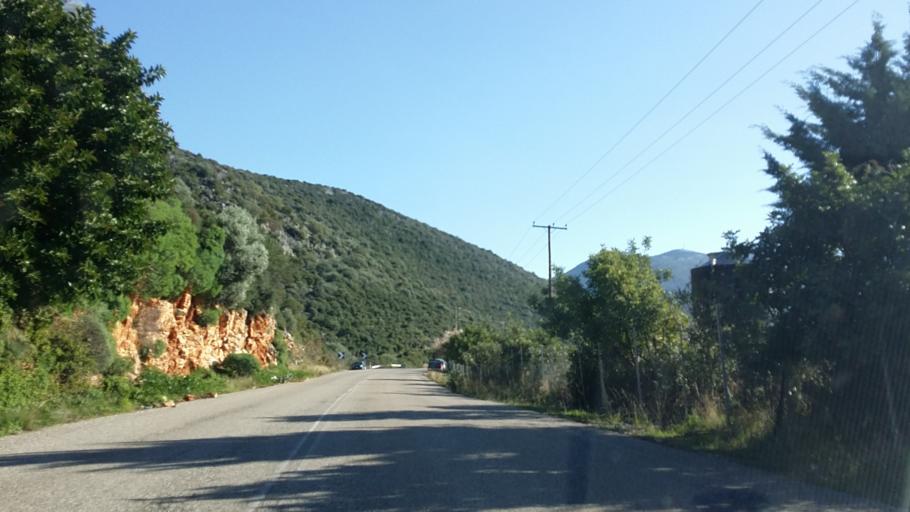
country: GR
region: West Greece
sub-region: Nomos Aitolias kai Akarnanias
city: Archontochorion
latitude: 38.6146
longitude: 21.0160
